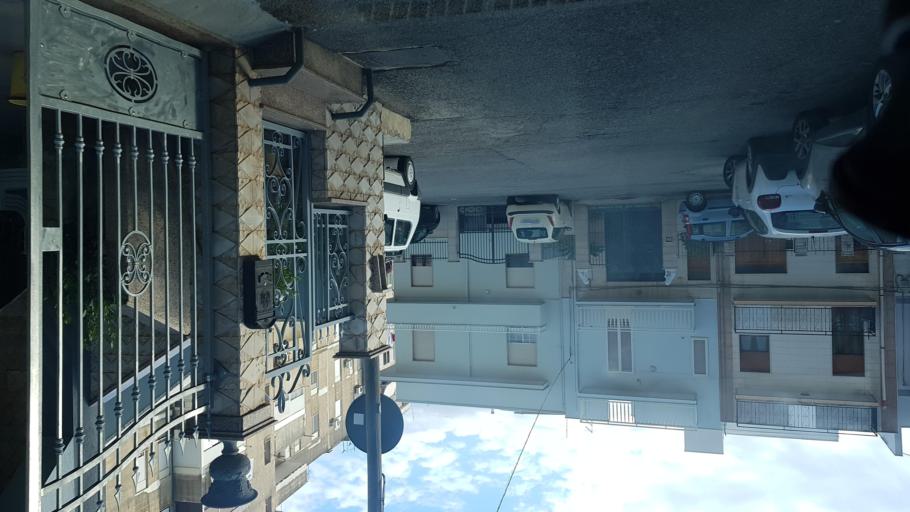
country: IT
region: Apulia
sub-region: Provincia di Brindisi
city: Francavilla Fontana
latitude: 40.5358
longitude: 17.5876
